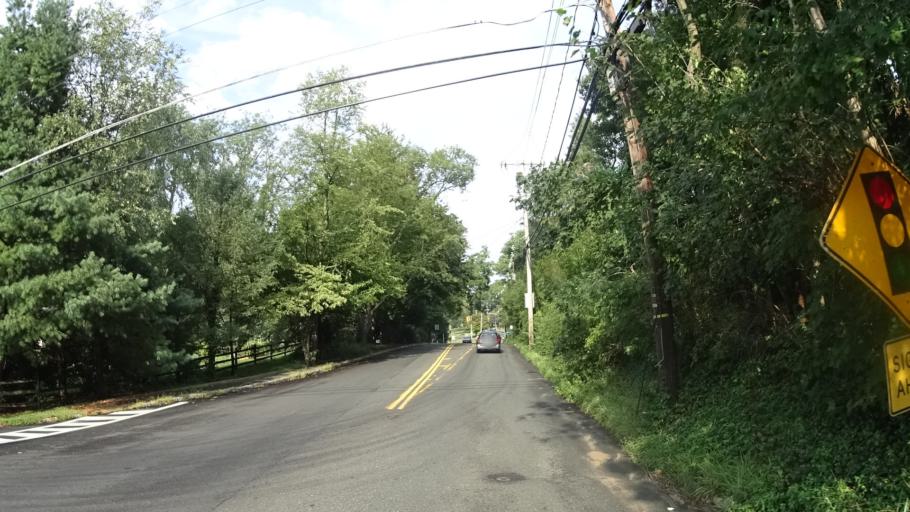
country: US
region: New Jersey
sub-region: Union County
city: New Providence
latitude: 40.7216
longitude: -74.4055
